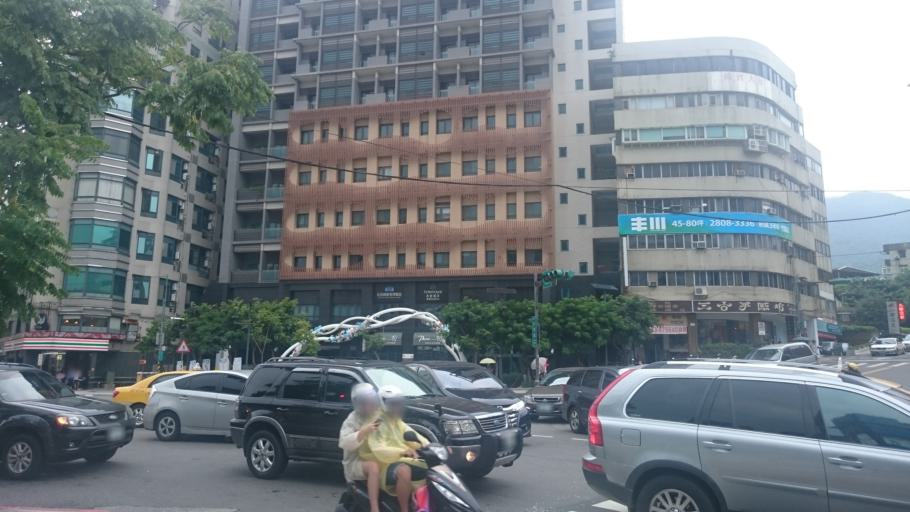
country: TW
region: Taipei
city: Taipei
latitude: 25.1370
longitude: 121.5038
